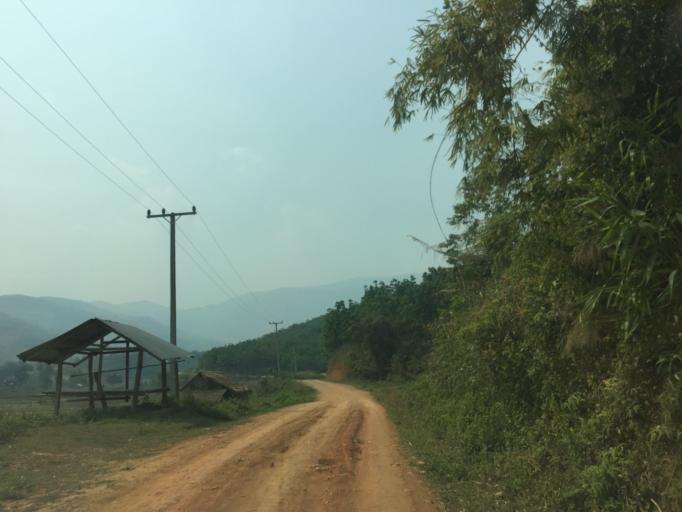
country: TH
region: Phayao
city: Phu Sang
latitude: 19.5749
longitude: 100.5257
